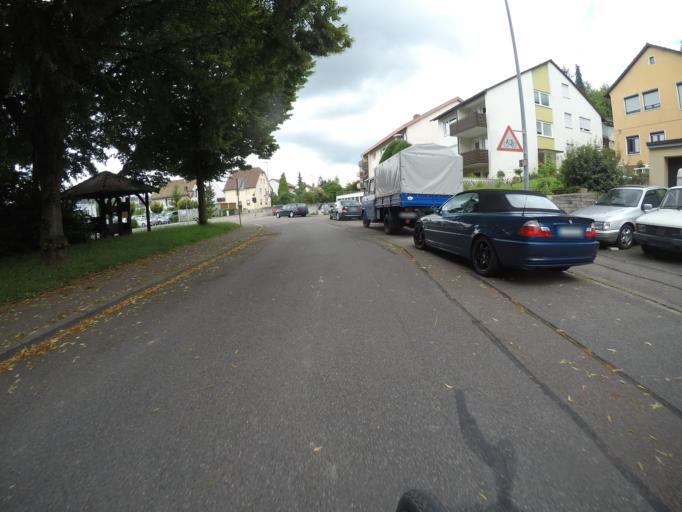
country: DE
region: Baden-Wuerttemberg
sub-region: Regierungsbezirk Stuttgart
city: Altbach
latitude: 48.7266
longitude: 9.3507
